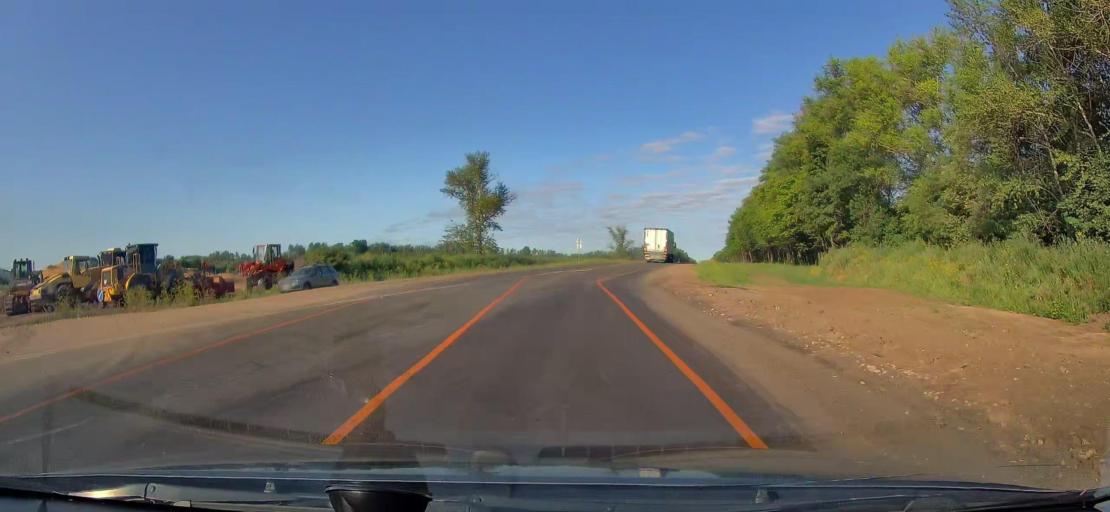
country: RU
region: Tula
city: Bol'shoye Skuratovo
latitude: 53.4431
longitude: 36.8326
